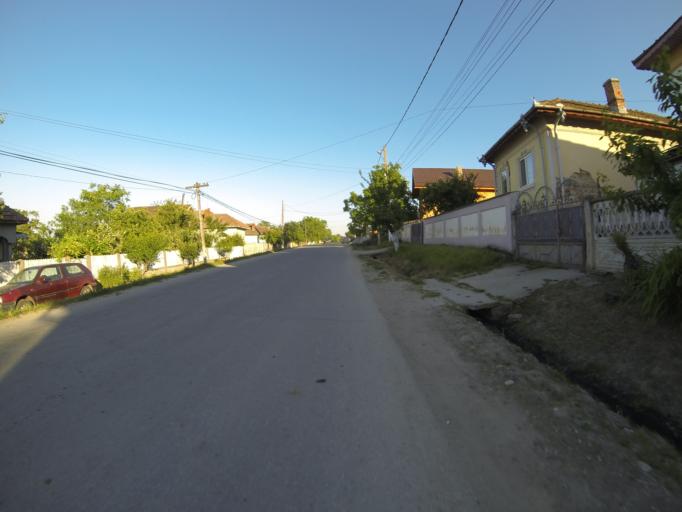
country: RO
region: Dolj
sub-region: Comuna Tuglui
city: Tuglui
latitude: 44.1994
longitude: 23.8009
